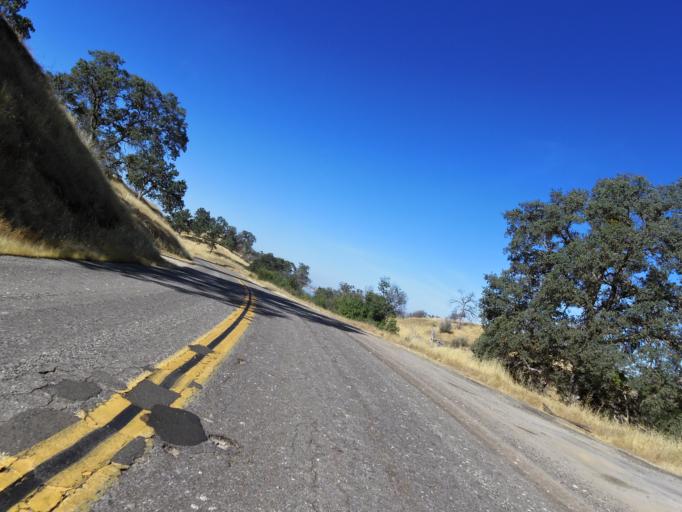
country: US
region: California
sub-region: Madera County
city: Yosemite Lakes
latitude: 37.1540
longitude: -119.8499
